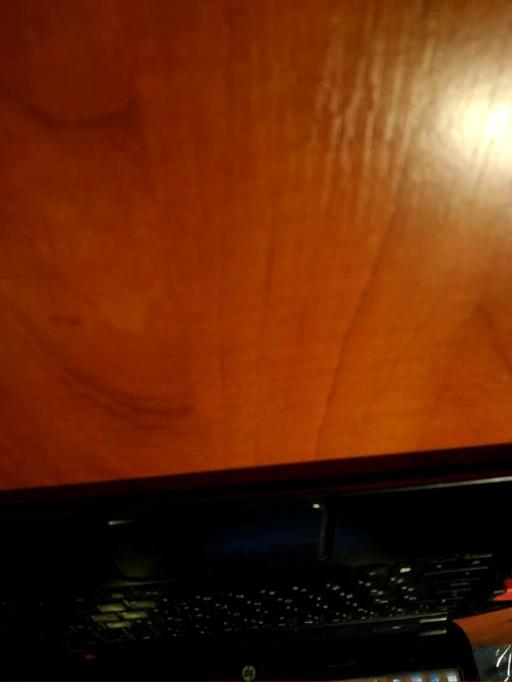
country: RU
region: Tverskaya
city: Zubtsov
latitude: 56.3180
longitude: 34.6782
